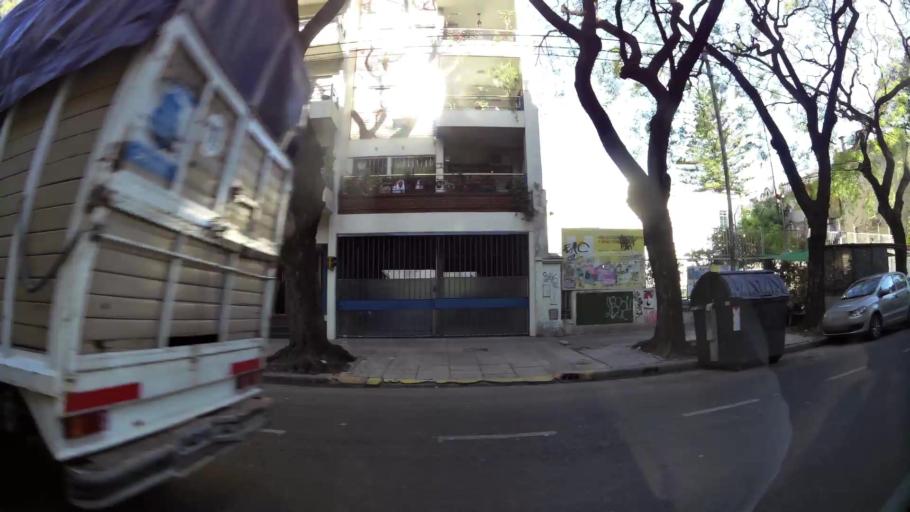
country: AR
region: Buenos Aires F.D.
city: Villa Santa Rita
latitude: -34.6240
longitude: -58.4345
